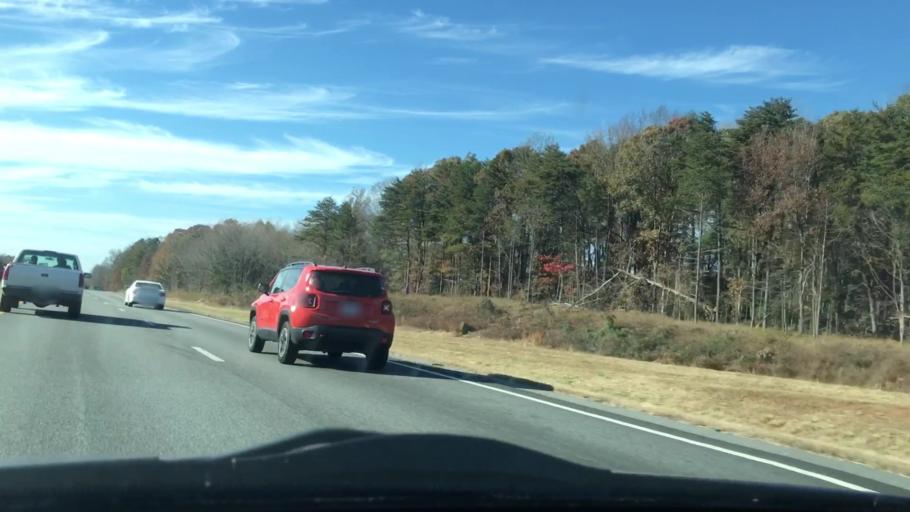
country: US
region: North Carolina
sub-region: Davidson County
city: Wallburg
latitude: 36.0275
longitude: -80.0608
